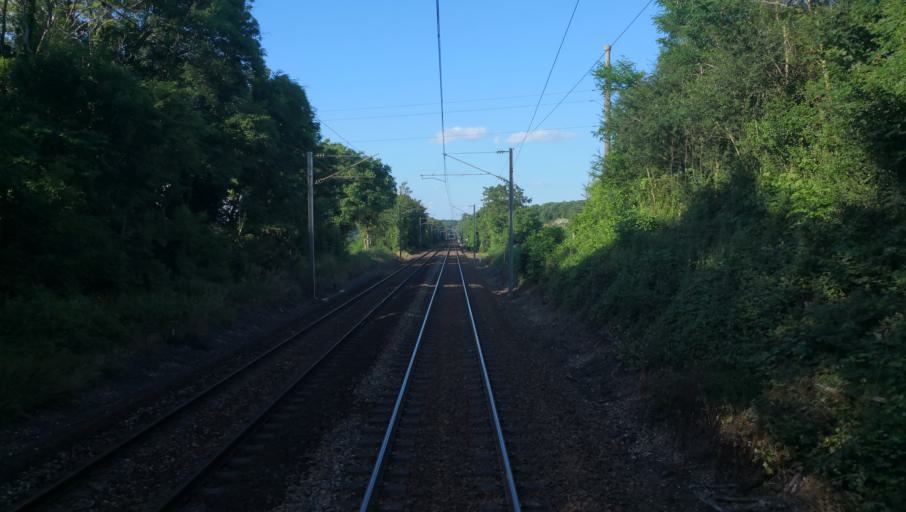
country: FR
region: Ile-de-France
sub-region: Departement des Yvelines
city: Rosny-sur-Seine
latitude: 48.9709
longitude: 1.6068
